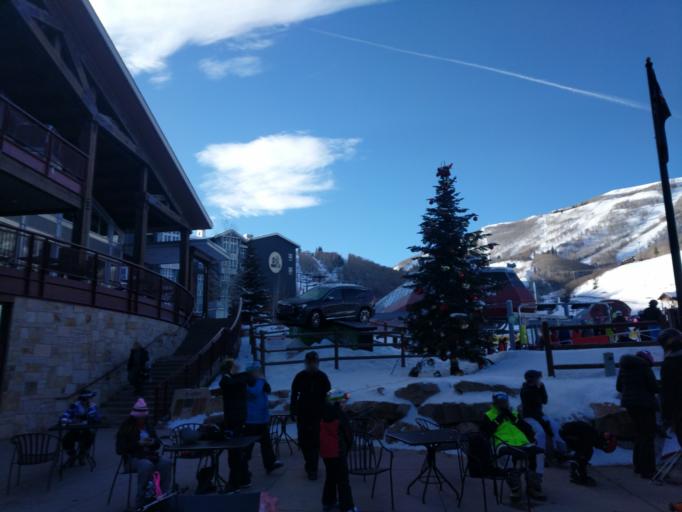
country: US
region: Utah
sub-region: Summit County
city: Park City
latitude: 40.6515
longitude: -111.5079
